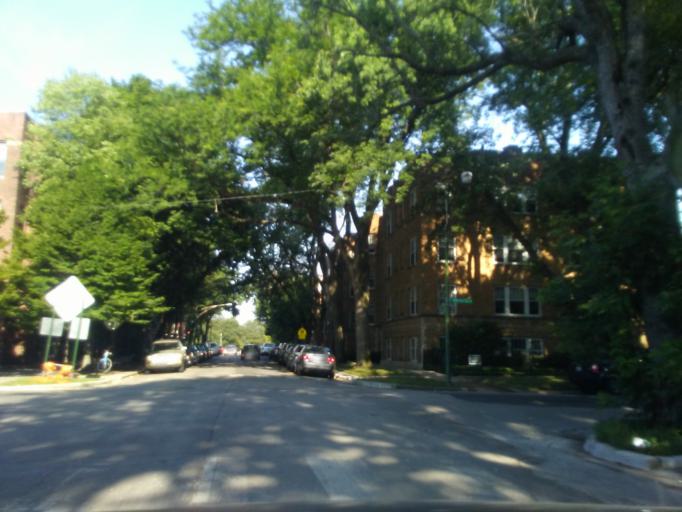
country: US
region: Illinois
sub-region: Cook County
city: Lincolnwood
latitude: 41.9733
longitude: -87.6777
